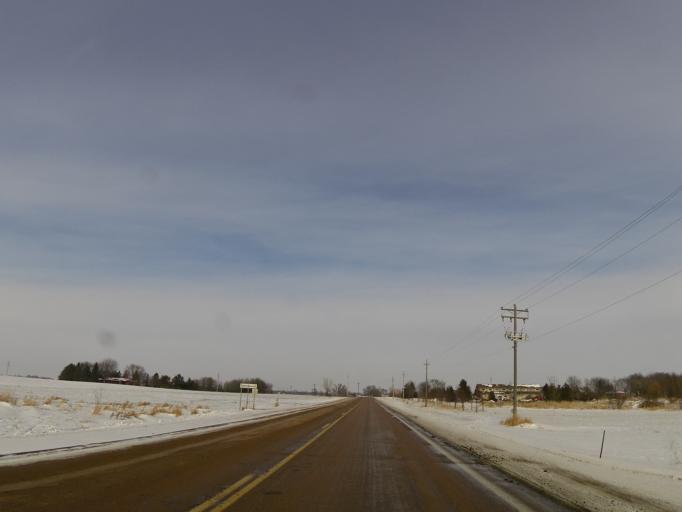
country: US
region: Minnesota
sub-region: McLeod County
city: Lester Prairie
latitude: 44.8879
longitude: -93.9703
